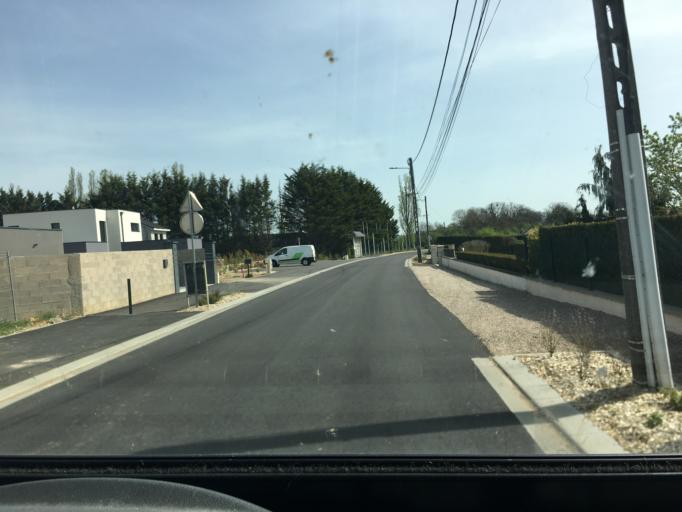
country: FR
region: Lorraine
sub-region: Departement de Meurthe-et-Moselle
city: Gondreville
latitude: 48.6603
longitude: 5.9827
